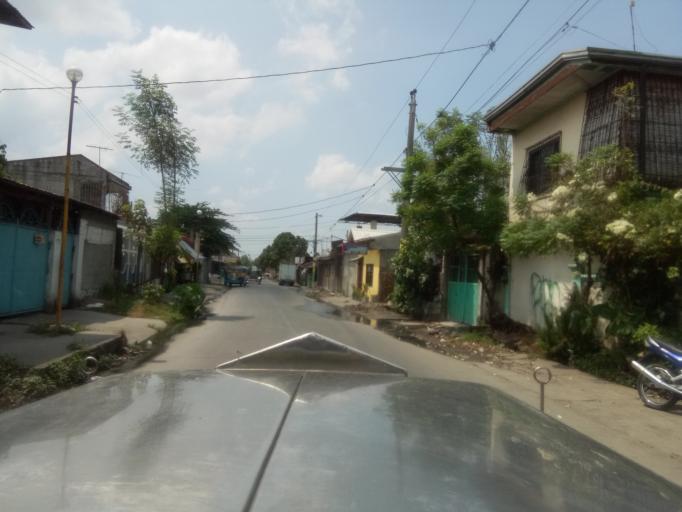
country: PH
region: Calabarzon
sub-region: Province of Cavite
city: Bulihan
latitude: 14.3153
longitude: 120.9766
